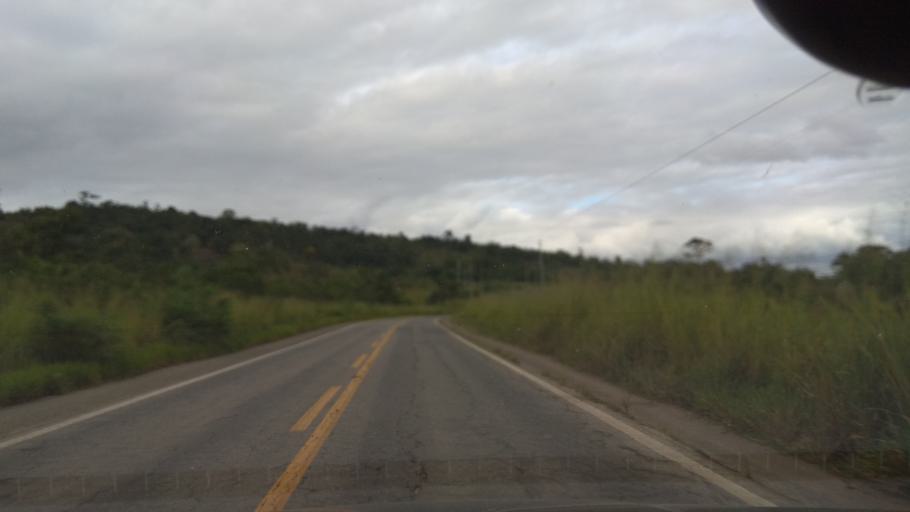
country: BR
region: Bahia
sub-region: Ipiau
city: Ipiau
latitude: -14.1477
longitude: -39.7039
